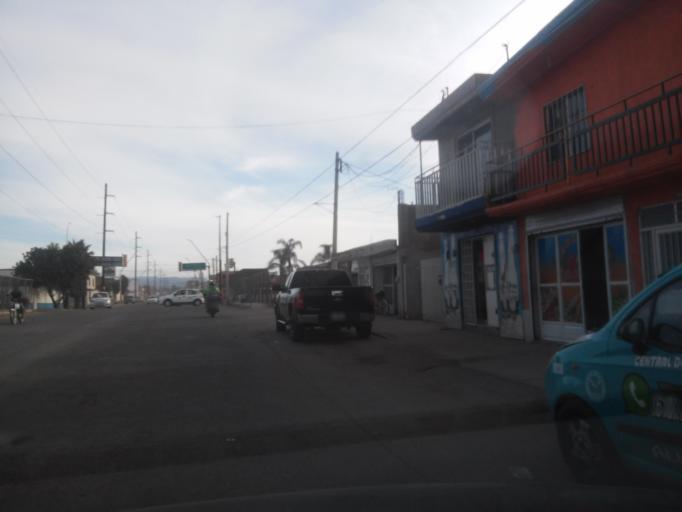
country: MX
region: Durango
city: Victoria de Durango
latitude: 24.0179
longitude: -104.6328
